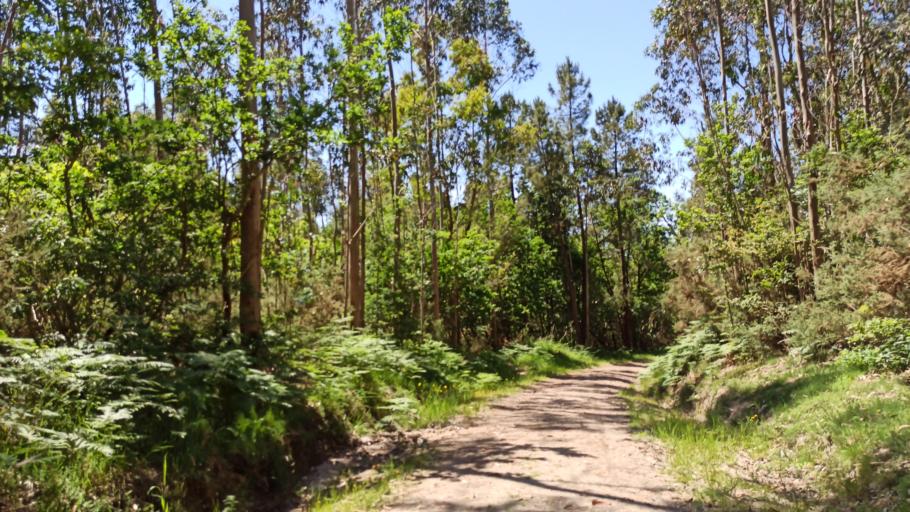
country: ES
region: Galicia
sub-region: Provincia da Coruna
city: Negreira
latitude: 42.9218
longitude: -8.7176
